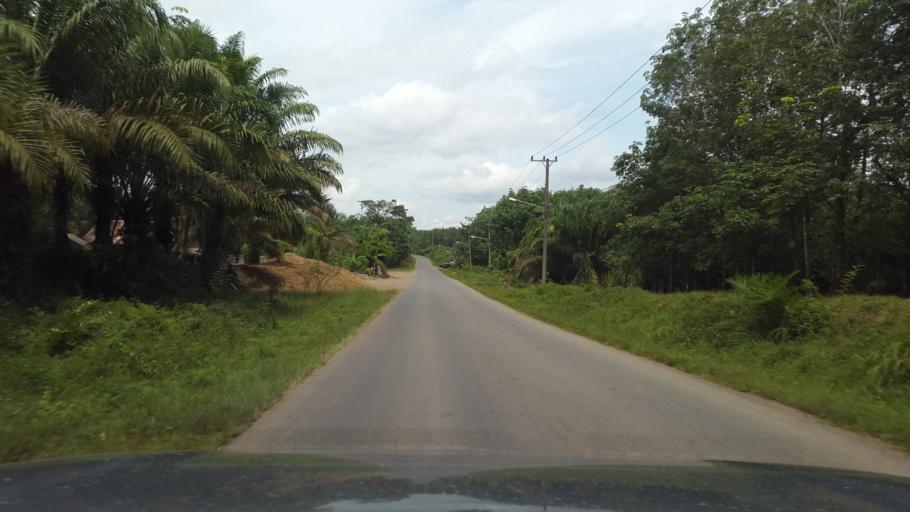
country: ID
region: South Sumatra
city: Gunungmegang Dalam
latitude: -3.3701
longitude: 103.9430
